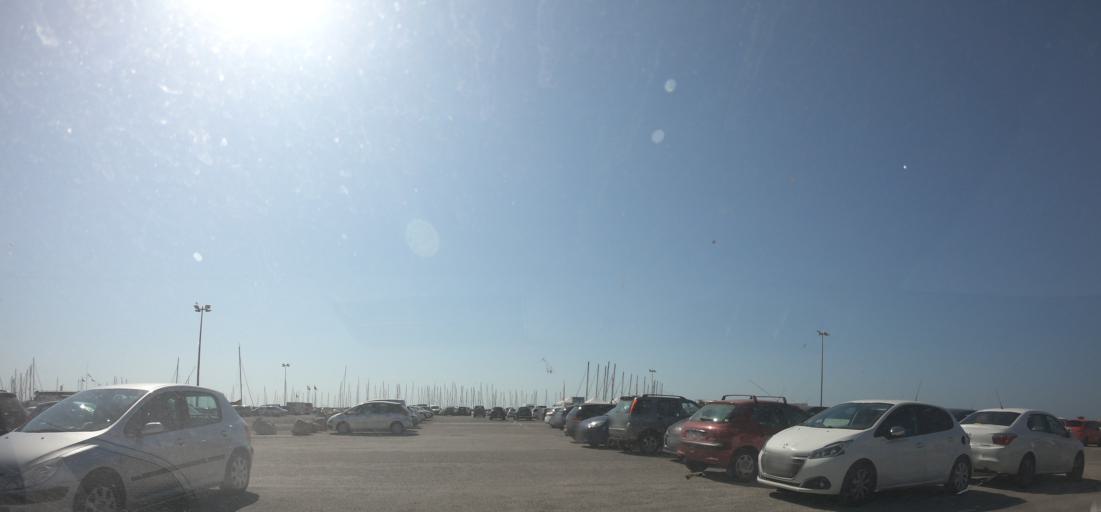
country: FR
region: Languedoc-Roussillon
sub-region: Departement de l'Herault
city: La Grande-Motte
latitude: 43.5572
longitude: 4.0792
